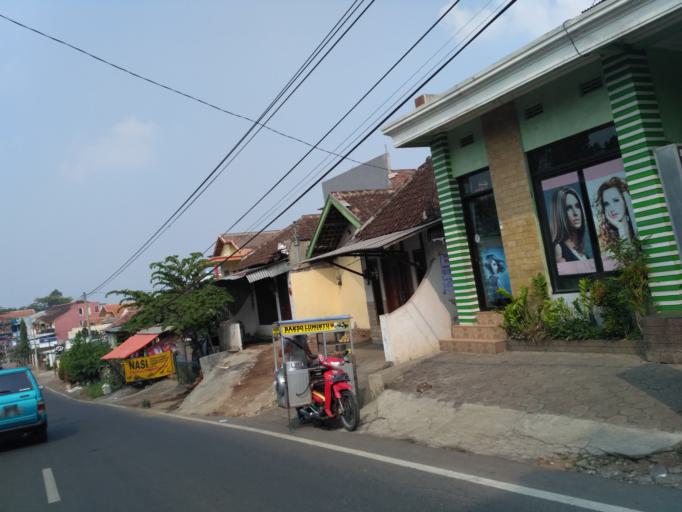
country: ID
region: East Java
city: Batu
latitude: -7.8644
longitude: 112.5379
